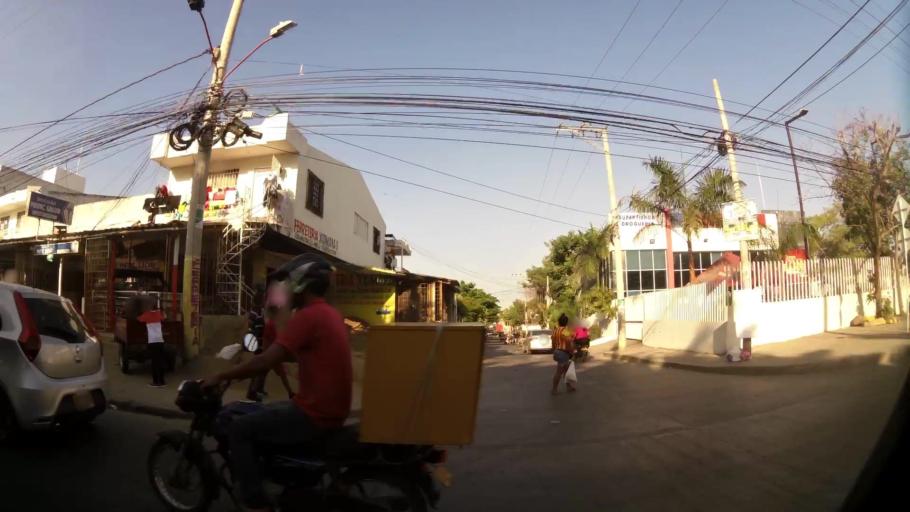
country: CO
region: Bolivar
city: Cartagena
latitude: 10.4022
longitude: -75.4824
